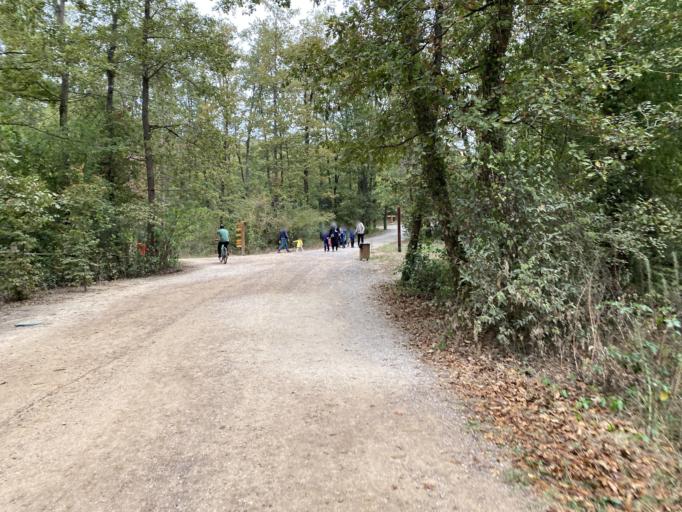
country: TR
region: Kocaeli
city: Derbent
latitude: 40.7371
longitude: 30.1669
